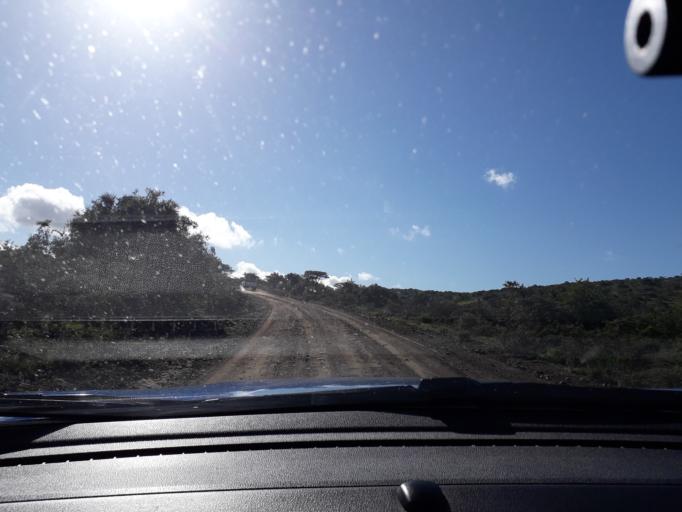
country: ZA
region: Eastern Cape
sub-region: Buffalo City Metropolitan Municipality
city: Bhisho
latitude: -33.1237
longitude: 27.4505
